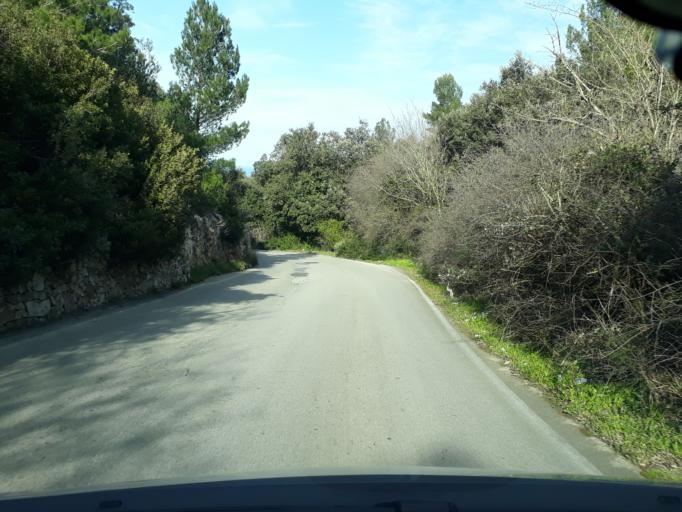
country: IT
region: Apulia
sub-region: Provincia di Brindisi
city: Lamie di Olimpie-Selva
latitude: 40.8040
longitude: 17.3522
